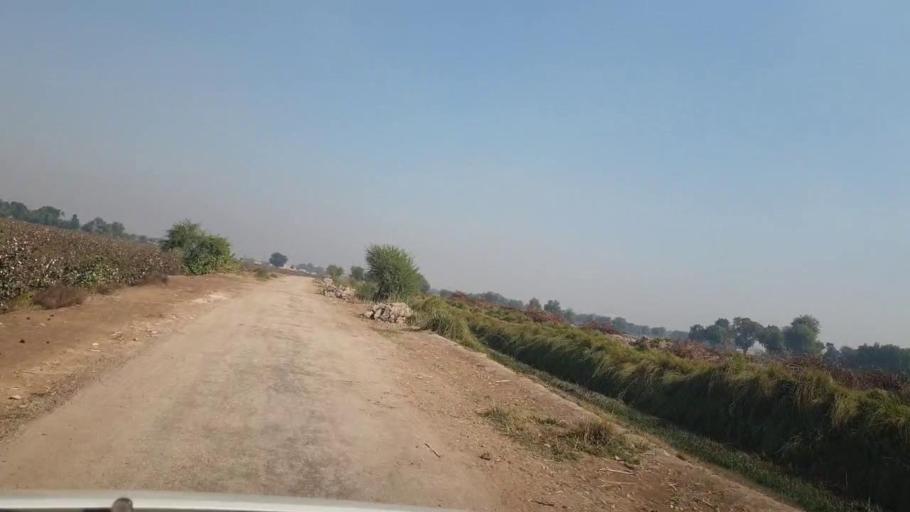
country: PK
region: Sindh
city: Bhan
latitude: 26.6178
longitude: 67.7616
